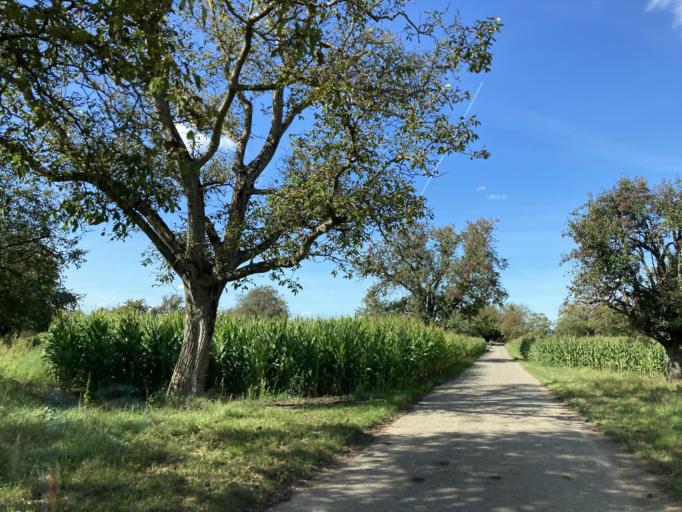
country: DE
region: Baden-Wuerttemberg
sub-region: Freiburg Region
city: Mullheim
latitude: 47.8125
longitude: 7.6473
